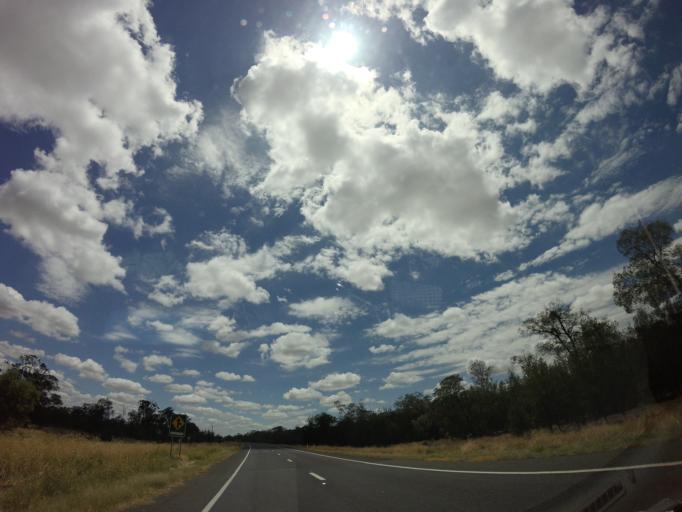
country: AU
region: New South Wales
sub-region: Moree Plains
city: Boggabilla
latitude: -28.9205
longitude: 150.1269
